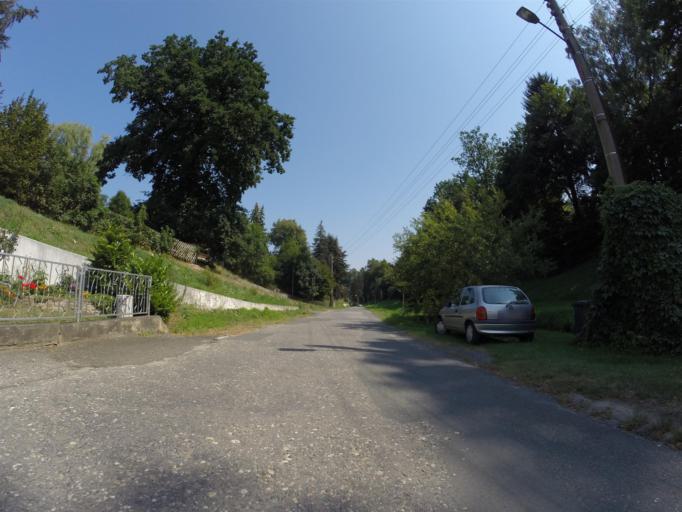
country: DE
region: Thuringia
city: Stadtroda
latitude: 50.8563
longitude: 11.7176
